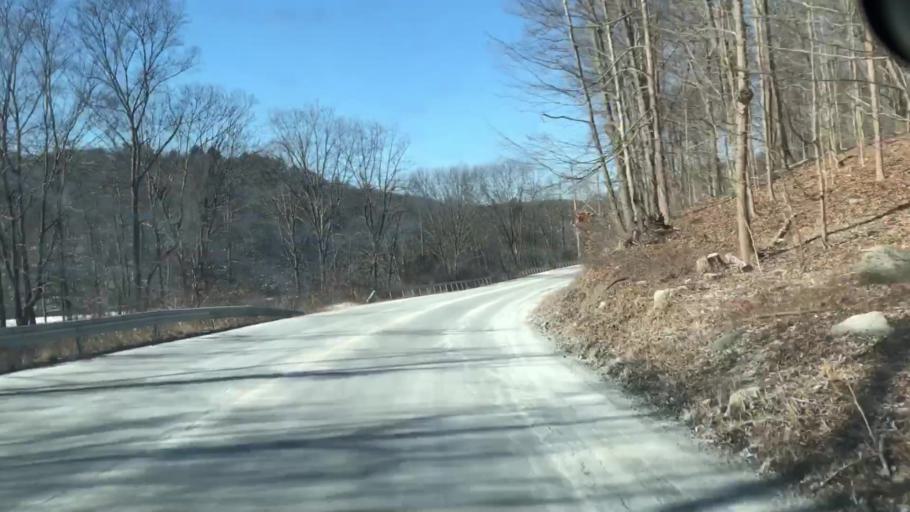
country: US
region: New York
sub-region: Putnam County
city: Carmel Hamlet
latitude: 41.3863
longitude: -73.6724
